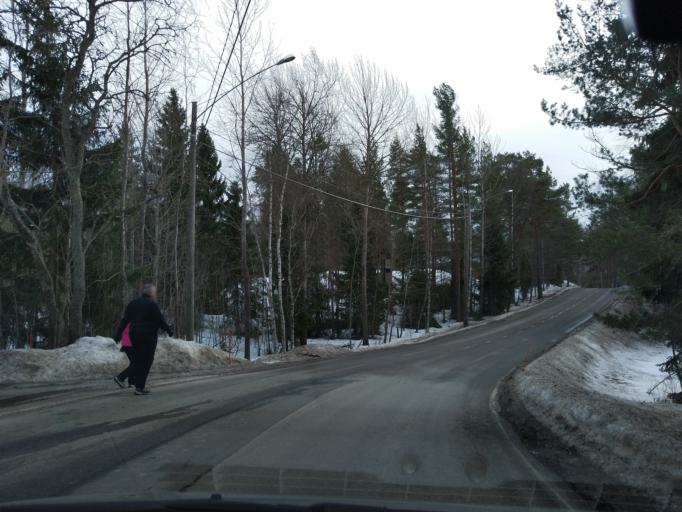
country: FI
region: Uusimaa
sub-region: Helsinki
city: Sibbo
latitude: 60.2685
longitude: 25.2861
